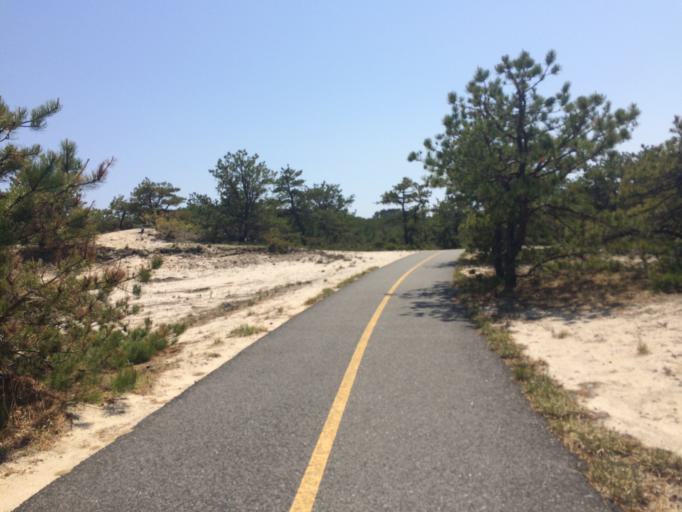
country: US
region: Massachusetts
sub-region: Barnstable County
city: Provincetown
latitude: 42.0642
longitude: -70.2155
